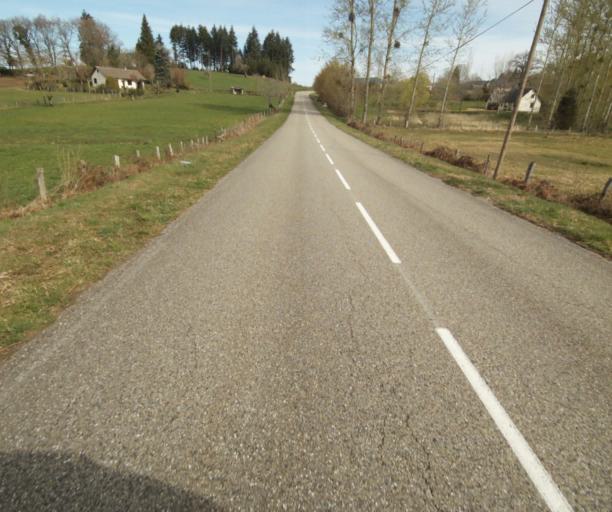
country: FR
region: Limousin
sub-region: Departement de la Correze
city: Correze
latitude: 45.4098
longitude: 1.8265
